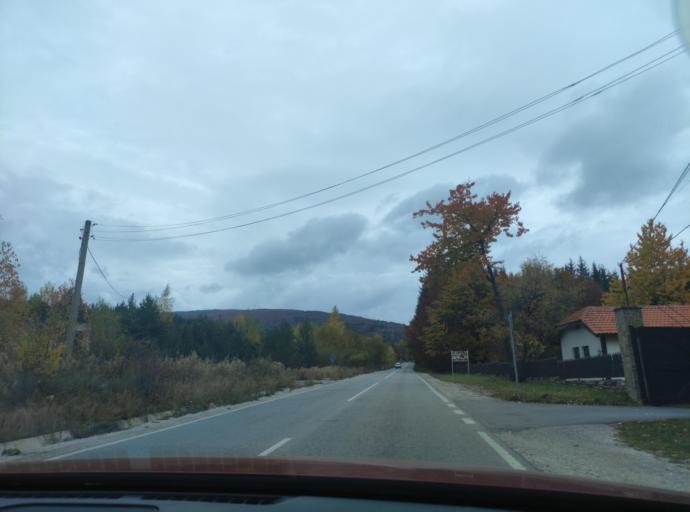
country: BG
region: Sofiya
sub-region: Obshtina Godech
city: Godech
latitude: 43.0987
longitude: 23.1010
